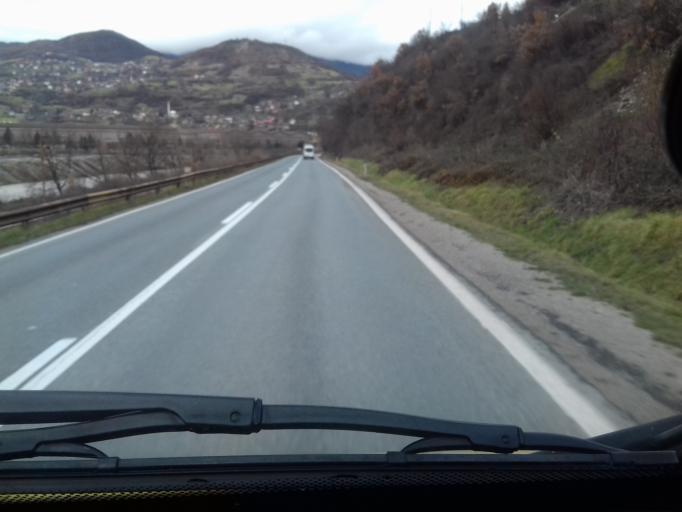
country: BA
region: Federation of Bosnia and Herzegovina
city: Zenica
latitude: 44.2340
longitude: 17.9018
